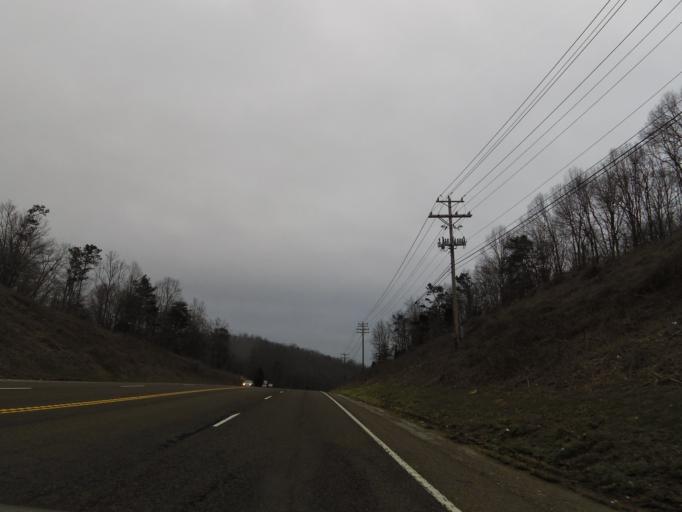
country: US
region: Tennessee
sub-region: Anderson County
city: Clinton
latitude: 36.0535
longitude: -84.1185
